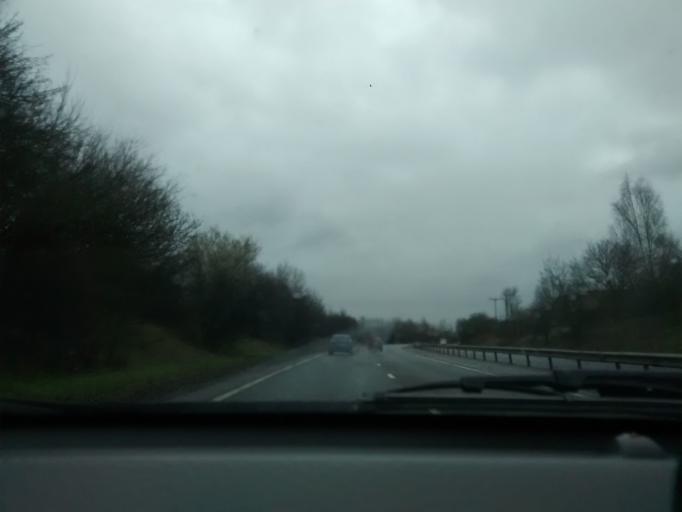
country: GB
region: England
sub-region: Suffolk
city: Stowmarket
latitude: 52.1949
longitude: 1.0113
